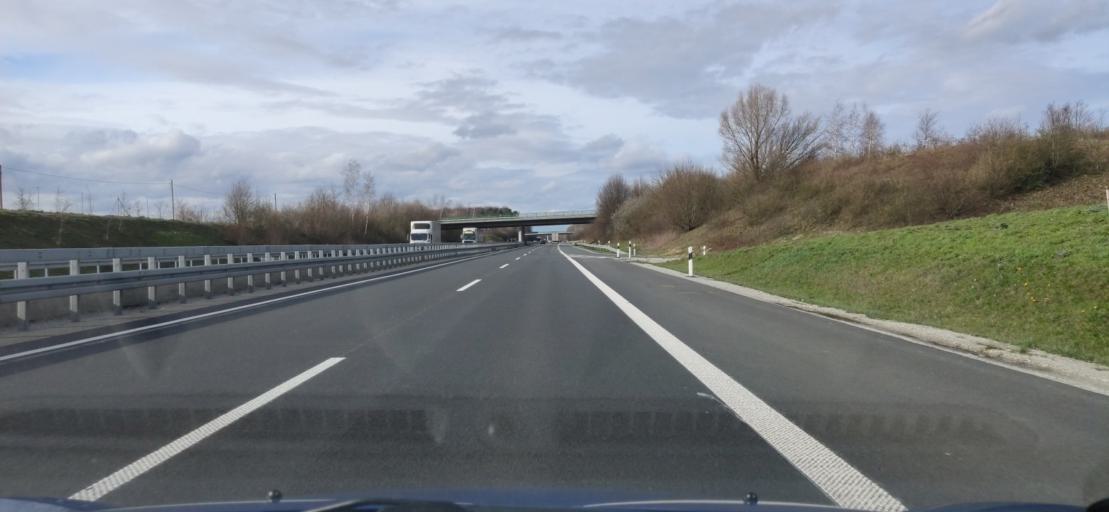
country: DE
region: North Rhine-Westphalia
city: Borgholzhausen
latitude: 52.0768
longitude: 8.2476
